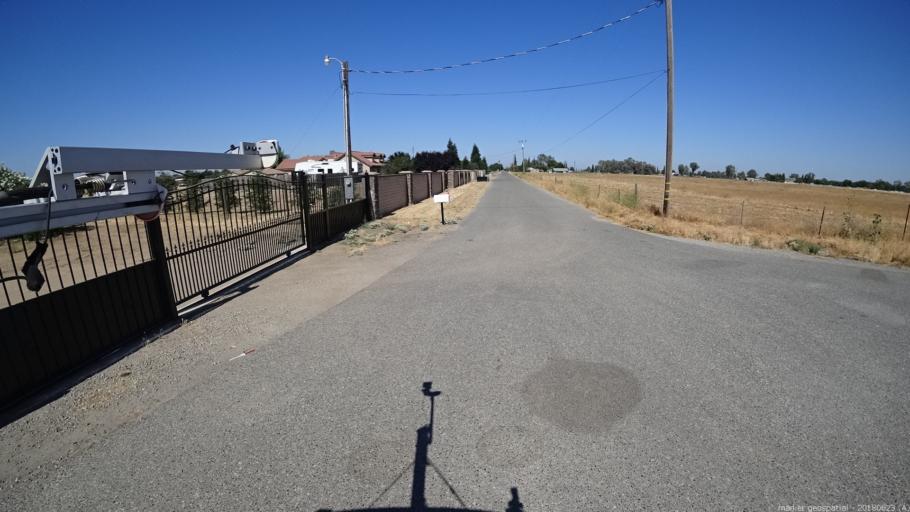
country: US
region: California
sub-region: Madera County
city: Parksdale
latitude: 36.9815
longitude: -120.0069
